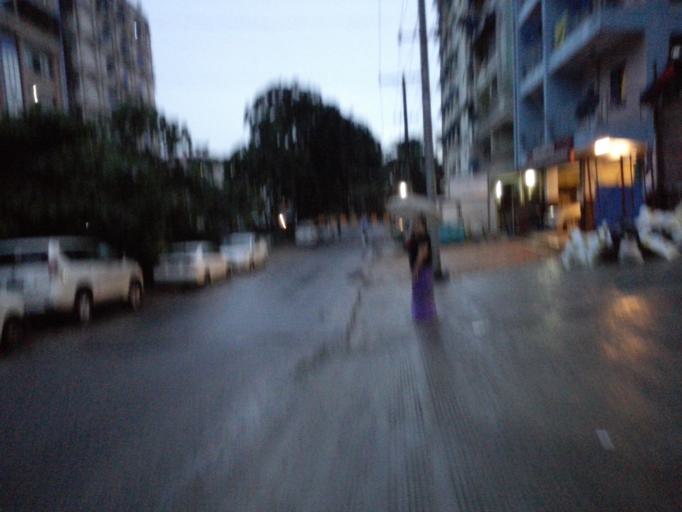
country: MM
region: Yangon
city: Yangon
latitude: 16.8265
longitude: 96.1720
